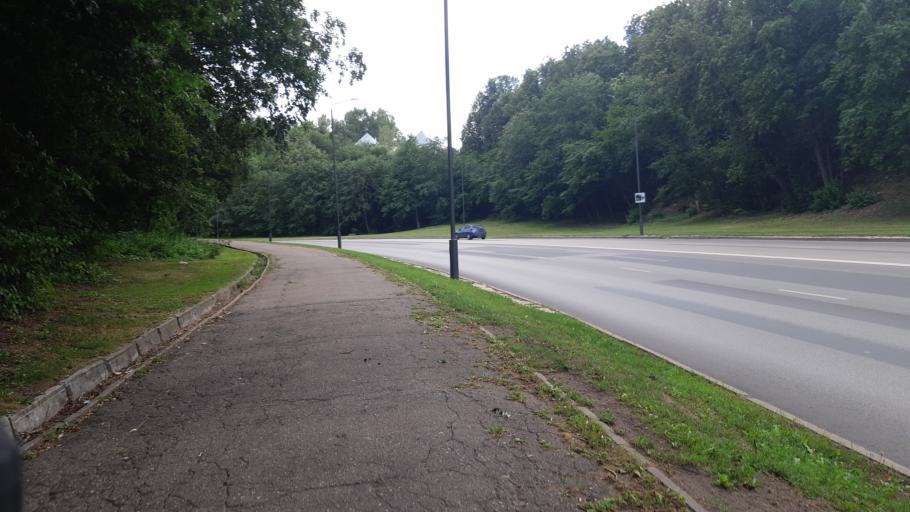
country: LT
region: Kauno apskritis
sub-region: Kaunas
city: Eiguliai
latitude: 54.9289
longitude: 23.9199
